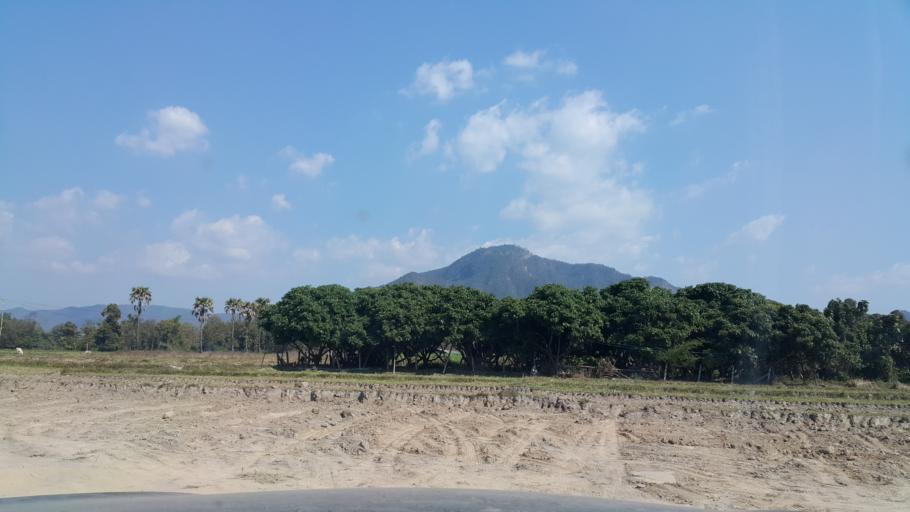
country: TH
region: Chiang Mai
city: Mae On
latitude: 18.7271
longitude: 99.2177
